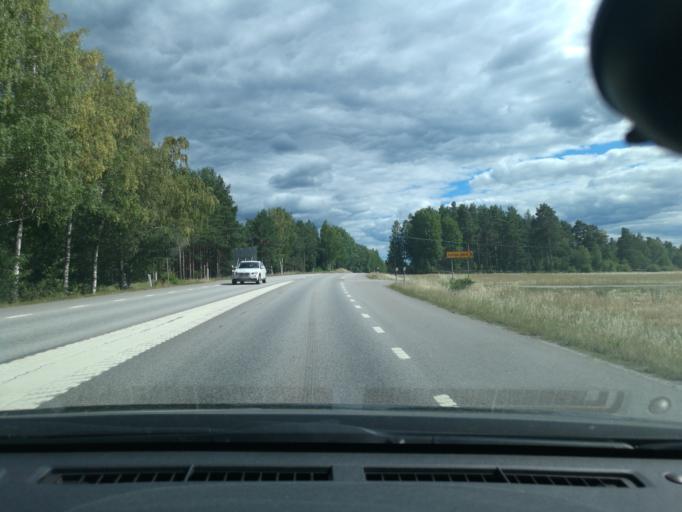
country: SE
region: OEstergoetland
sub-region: Soderkopings Kommun
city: Soederkoeping
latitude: 58.4612
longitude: 16.3625
